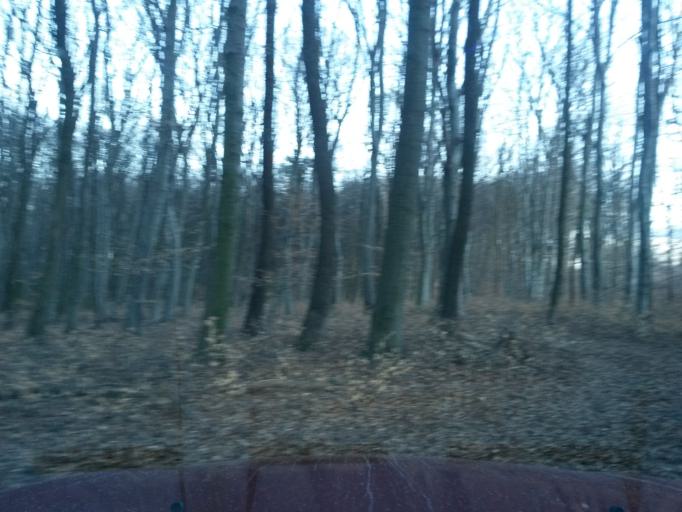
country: SK
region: Kosicky
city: Kosice
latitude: 48.7046
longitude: 21.3750
